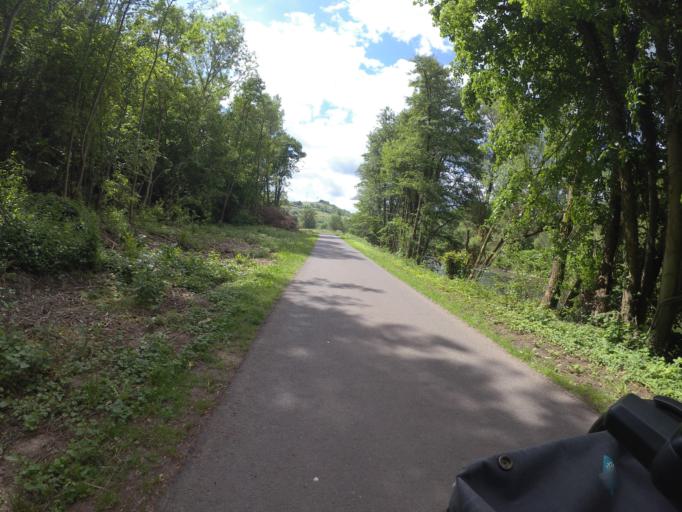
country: DE
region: Rheinland-Pfalz
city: Odernheim
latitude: 49.7815
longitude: 7.7114
